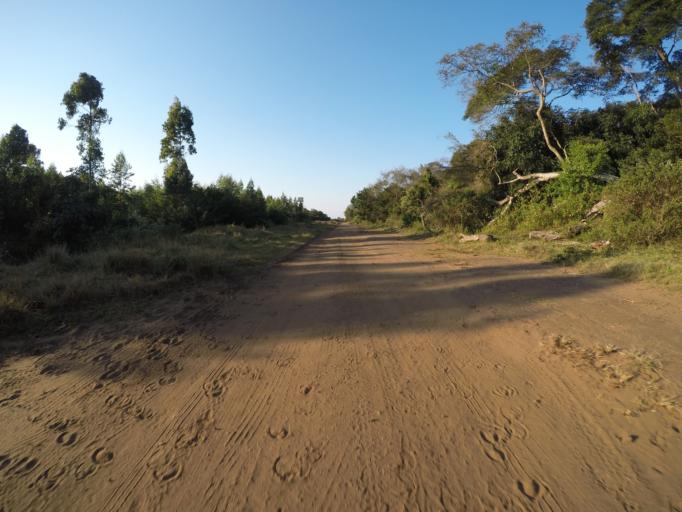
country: ZA
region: KwaZulu-Natal
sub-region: uThungulu District Municipality
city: KwaMbonambi
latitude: -28.6960
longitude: 32.1964
